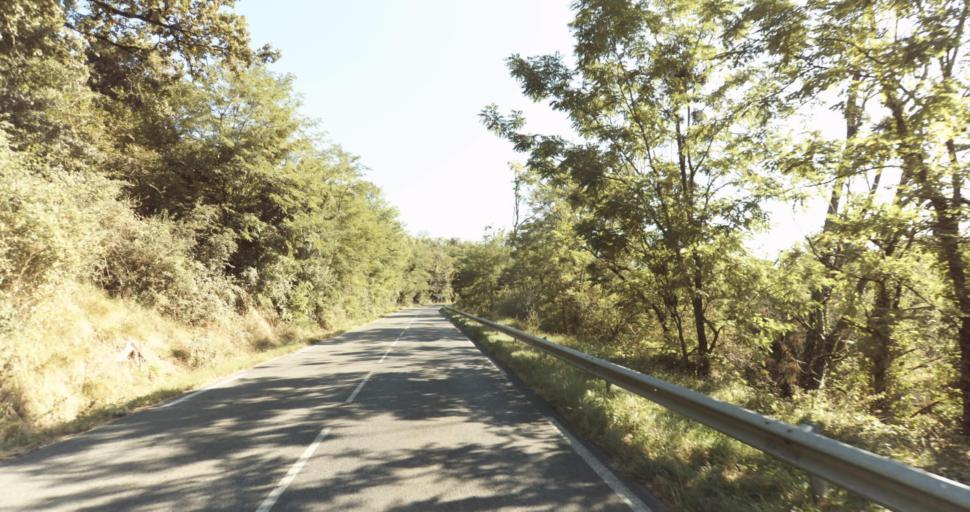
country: FR
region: Midi-Pyrenees
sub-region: Departement de la Haute-Garonne
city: L'Union
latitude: 43.6700
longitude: 1.4752
